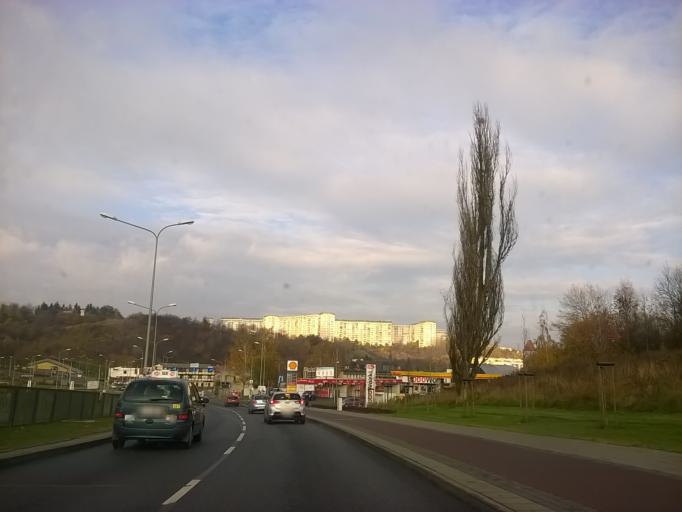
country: PL
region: Pomeranian Voivodeship
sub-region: Gdansk
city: Gdansk
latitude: 54.3454
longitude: 18.6033
